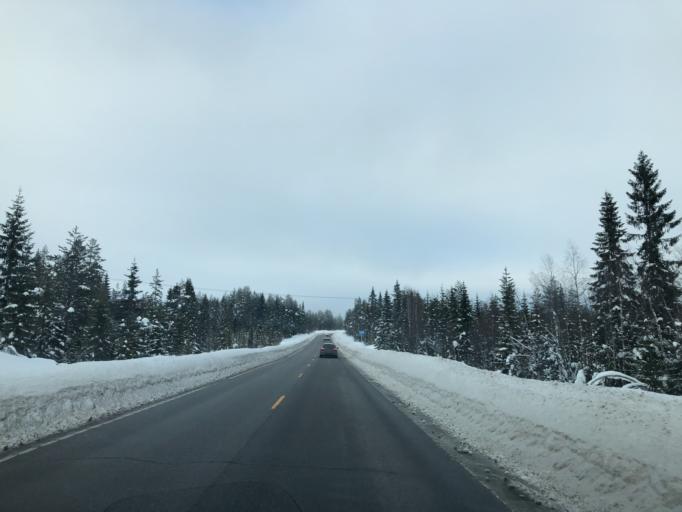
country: NO
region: Hedmark
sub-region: Trysil
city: Innbygda
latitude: 61.2298
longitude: 12.2517
